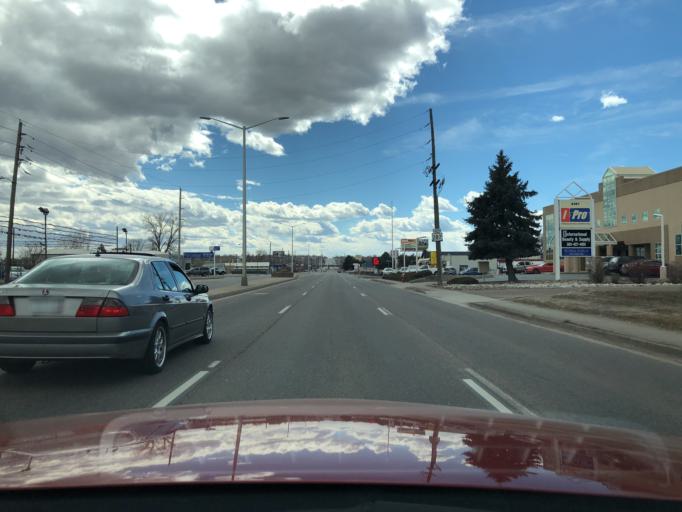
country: US
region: Colorado
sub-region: Adams County
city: Berkley
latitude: 39.8116
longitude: -105.0254
